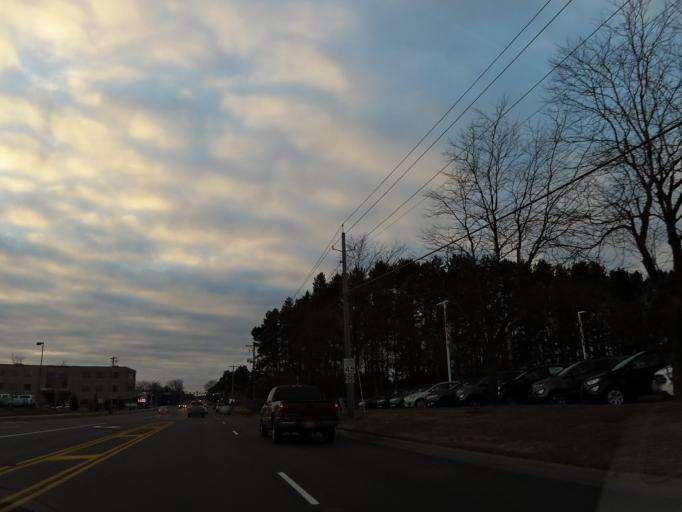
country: US
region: Minnesota
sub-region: Ramsey County
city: Vadnais Heights
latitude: 45.0504
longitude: -93.0384
